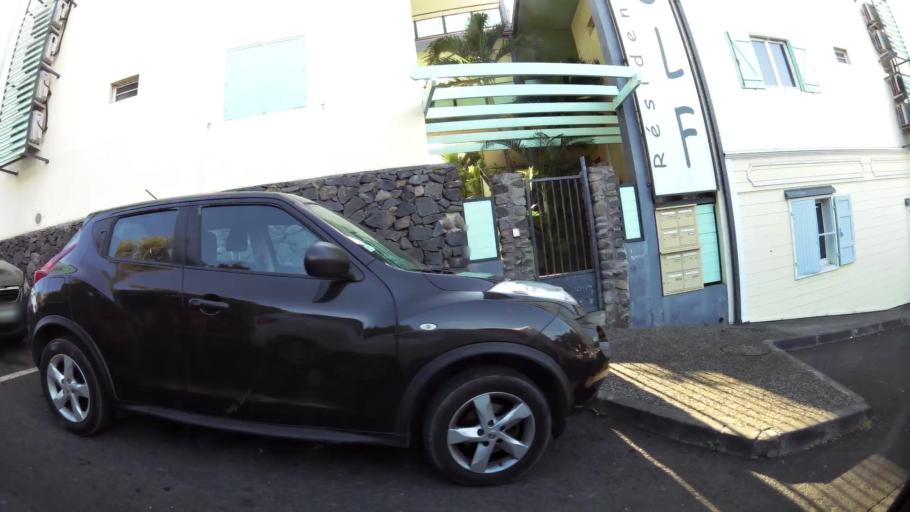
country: RE
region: Reunion
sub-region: Reunion
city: Les Avirons
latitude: -21.2632
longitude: 55.3623
